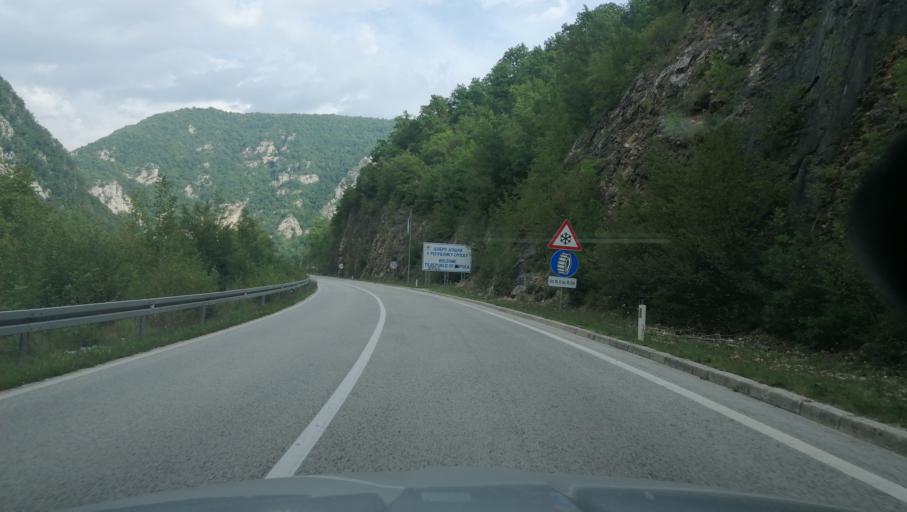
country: BA
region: Federation of Bosnia and Herzegovina
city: Jajce
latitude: 44.4577
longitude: 17.2388
